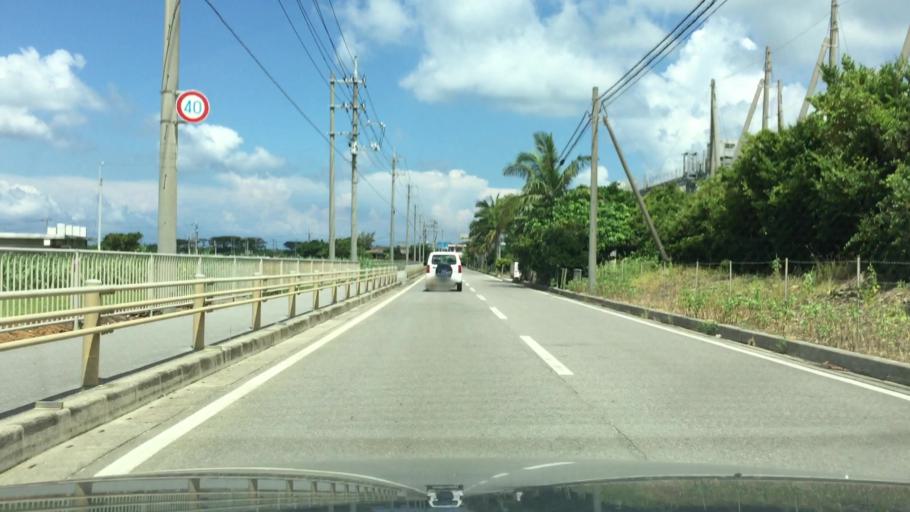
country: JP
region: Okinawa
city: Ishigaki
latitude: 24.3940
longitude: 124.1590
